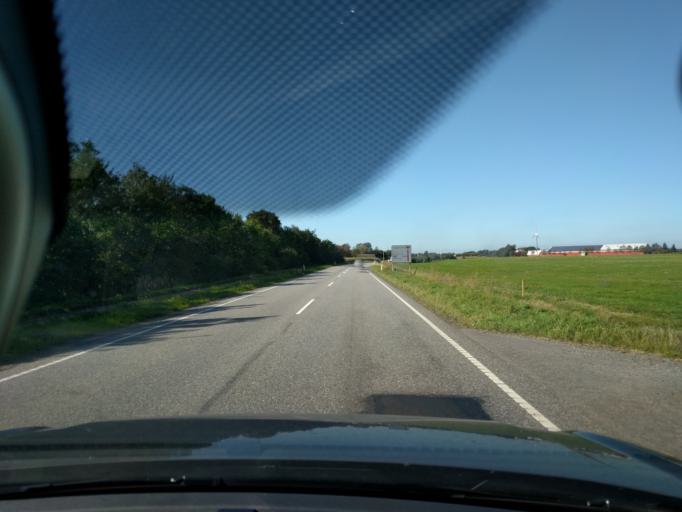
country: DK
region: North Denmark
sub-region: Mariagerfjord Kommune
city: Hobro
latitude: 56.6786
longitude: 9.6663
